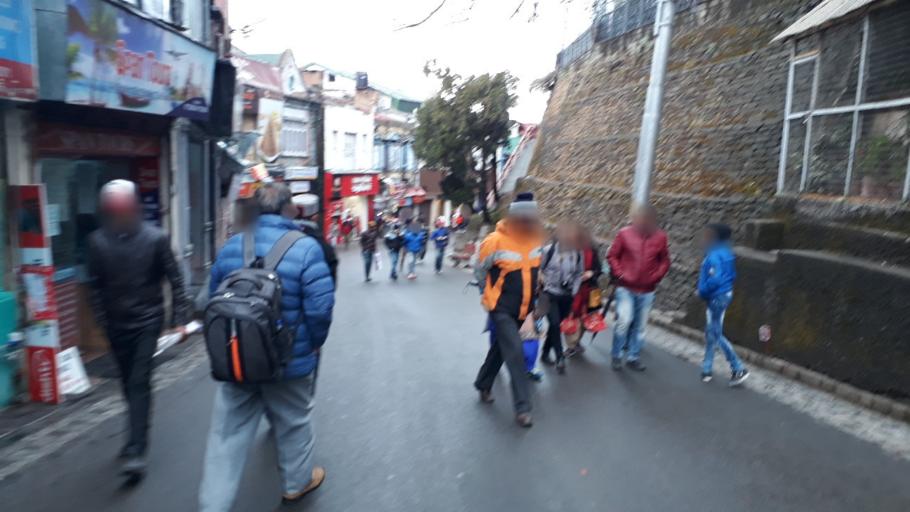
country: IN
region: Himachal Pradesh
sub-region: Shimla
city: Shimla
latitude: 31.1052
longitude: 77.1718
